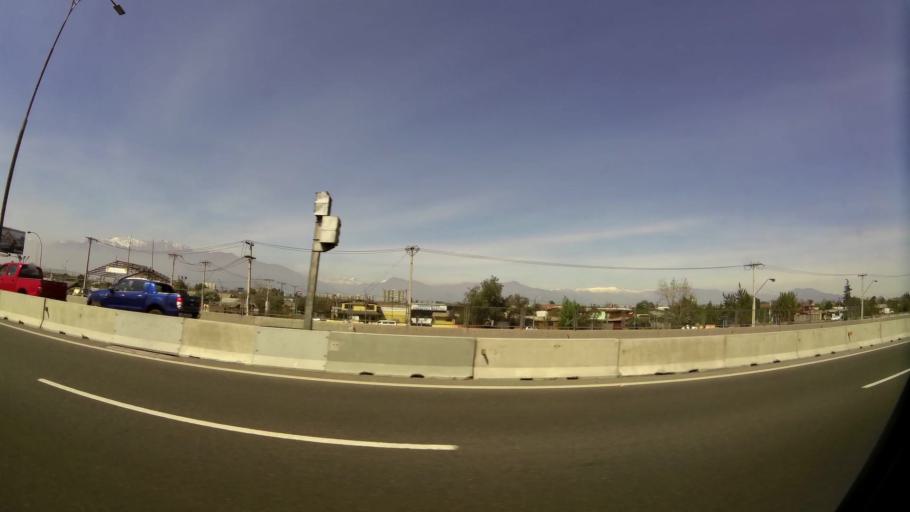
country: CL
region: Santiago Metropolitan
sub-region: Provincia de Maipo
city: San Bernardo
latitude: -33.5342
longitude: -70.6828
